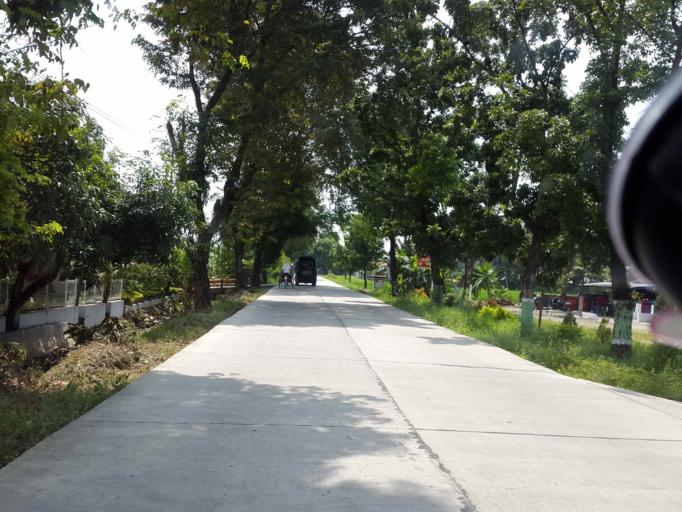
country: ID
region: Central Java
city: Pemalang
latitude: -6.9046
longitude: 109.3912
